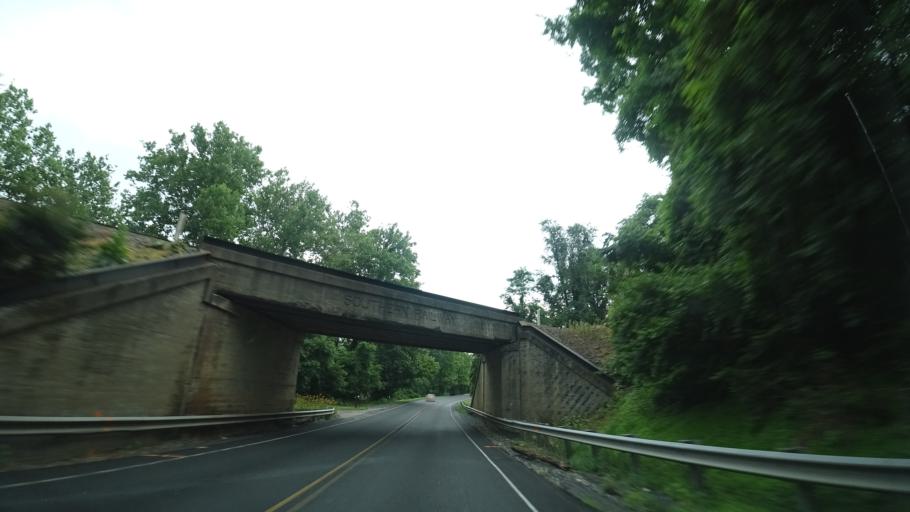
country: US
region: Virginia
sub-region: Warren County
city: Apple Mountain Lake
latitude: 38.9142
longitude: -78.1106
